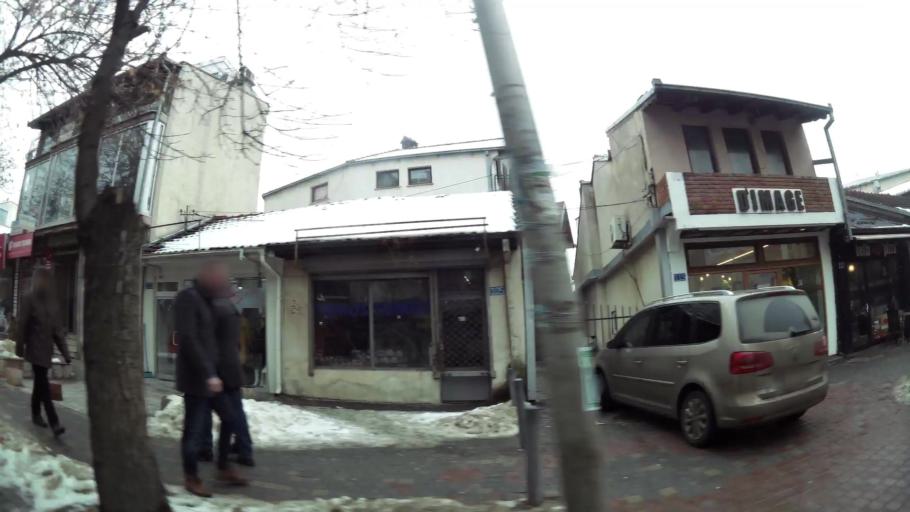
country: XK
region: Pristina
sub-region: Komuna e Prishtines
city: Pristina
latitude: 42.6657
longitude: 21.1632
